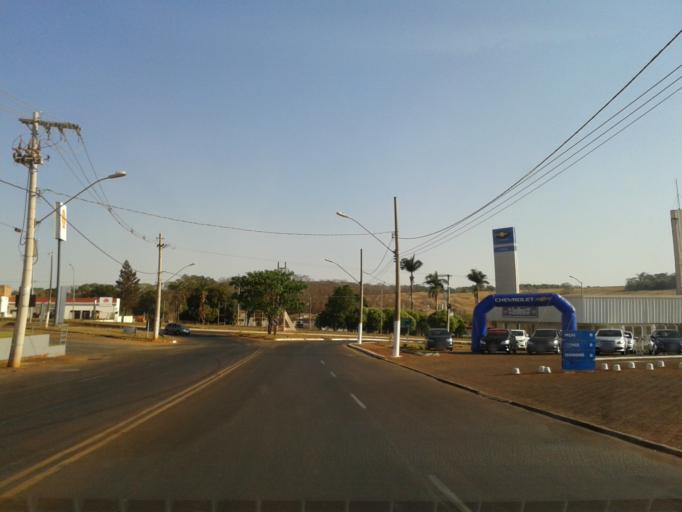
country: BR
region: Minas Gerais
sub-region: Ituiutaba
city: Ituiutaba
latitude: -18.9484
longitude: -49.4587
